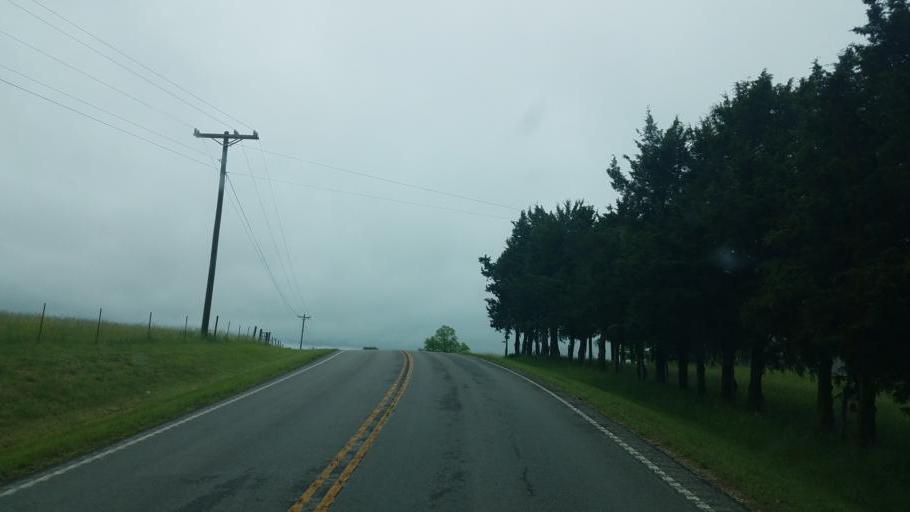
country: US
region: Missouri
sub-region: Miller County
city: Eldon
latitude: 38.4621
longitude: -92.5581
